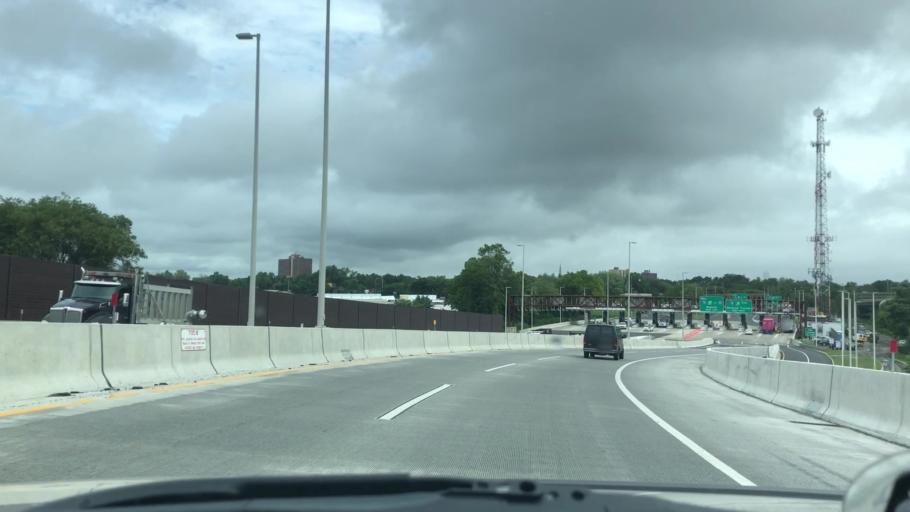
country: US
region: New Jersey
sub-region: Hudson County
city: Bayonne
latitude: 40.6821
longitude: -74.0992
